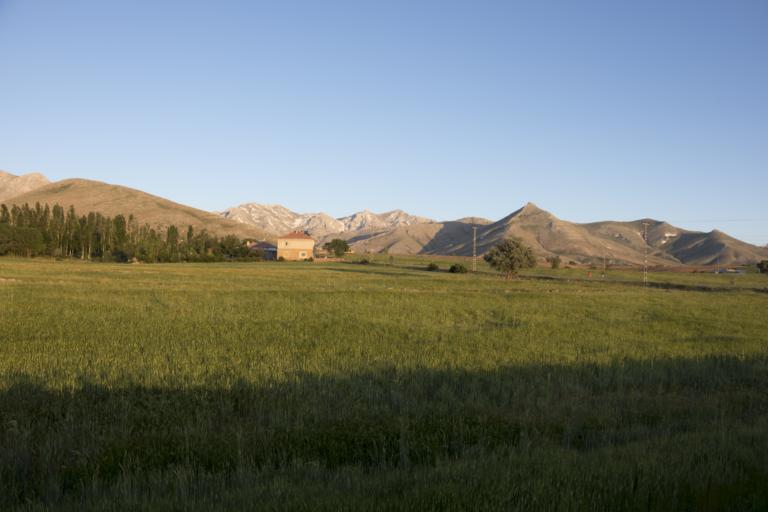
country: TR
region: Kayseri
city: Toklar
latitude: 38.4234
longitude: 36.0882
